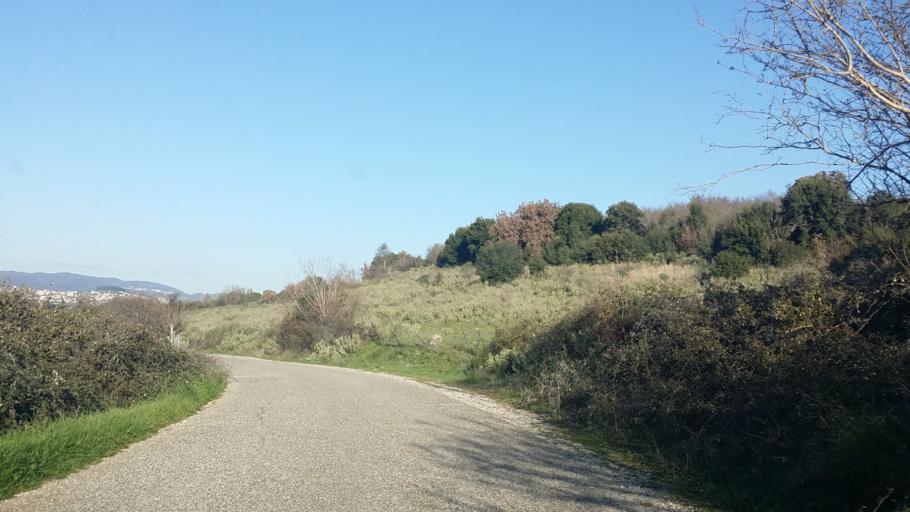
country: GR
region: West Greece
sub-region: Nomos Aitolias kai Akarnanias
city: Katouna
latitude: 38.7604
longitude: 21.1428
